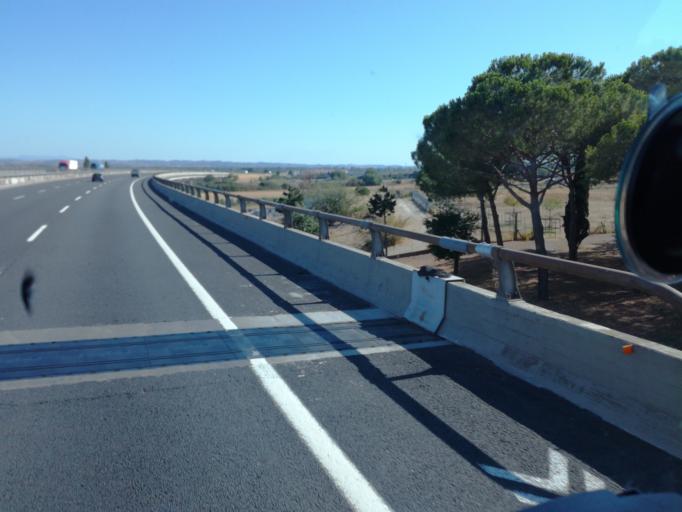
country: IT
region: Latium
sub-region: Citta metropolitana di Roma Capitale
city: Fiano Romano
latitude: 42.1535
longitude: 12.6244
